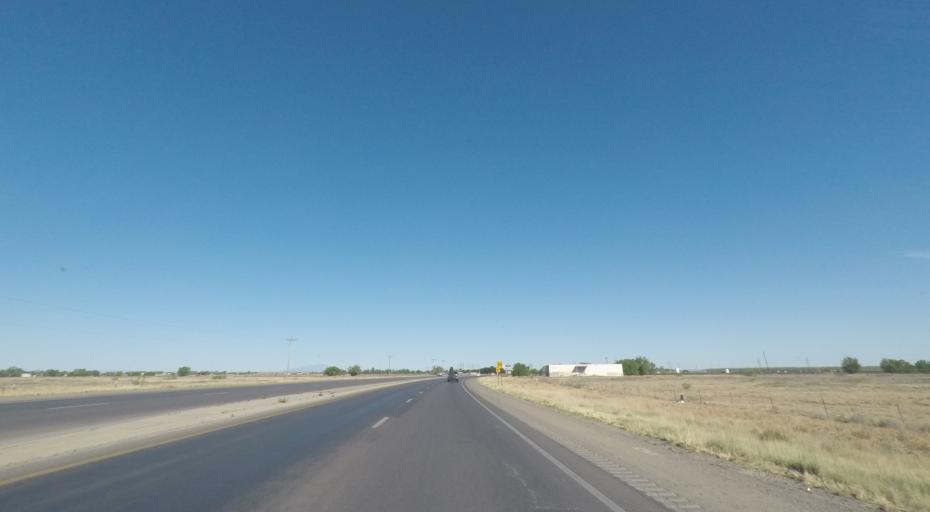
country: US
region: New Mexico
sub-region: Chaves County
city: Roswell
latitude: 33.3226
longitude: -104.4974
